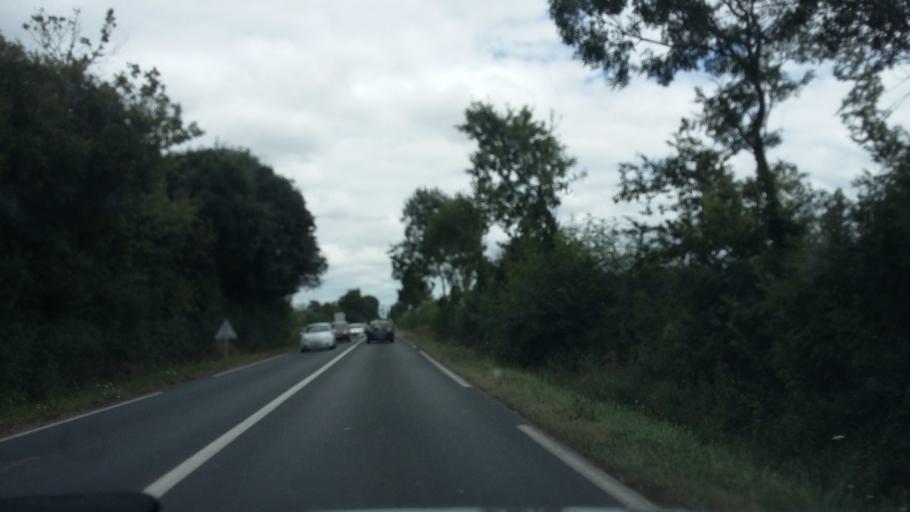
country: FR
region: Pays de la Loire
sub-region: Departement de la Vendee
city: Saint-Christophe-du-Ligneron
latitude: 46.8239
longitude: -1.7786
